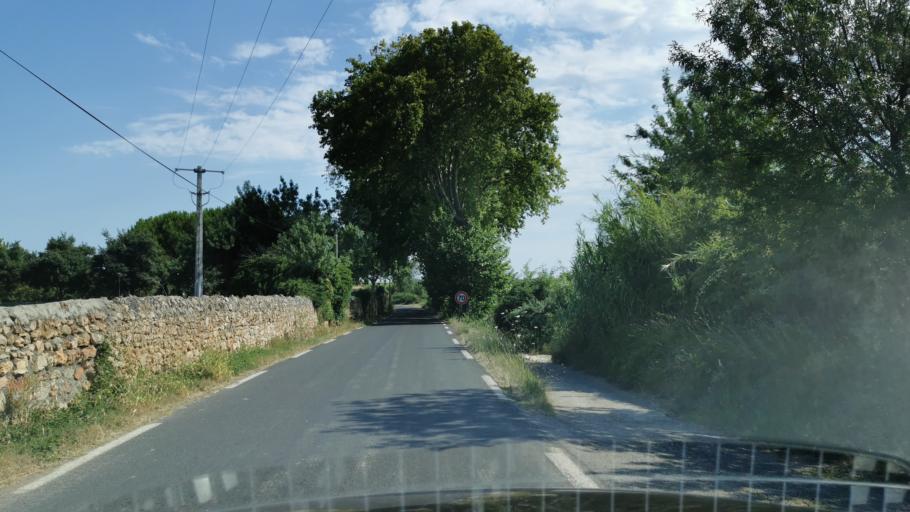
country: FR
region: Languedoc-Roussillon
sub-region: Departement de l'Herault
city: Cazouls-les-Beziers
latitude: 43.3837
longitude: 3.0998
